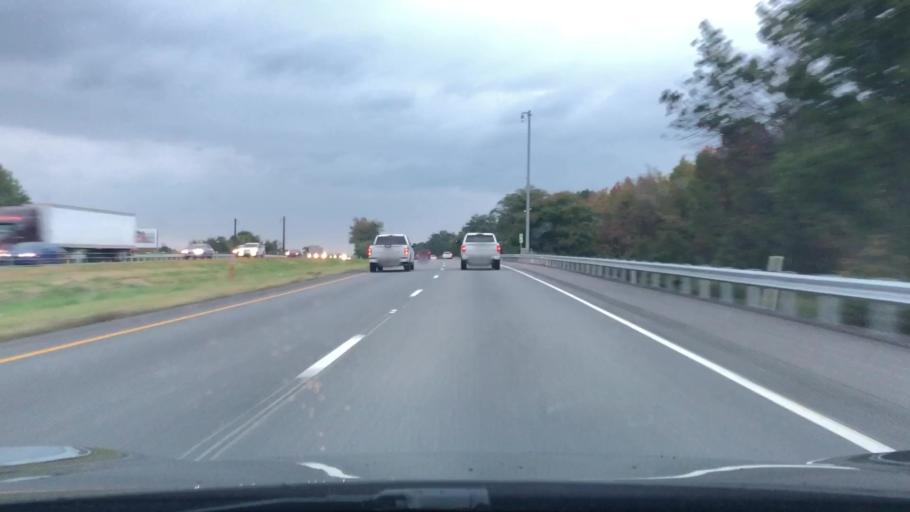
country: US
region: Pennsylvania
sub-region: Bucks County
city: Woodbourne
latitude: 40.2016
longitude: -74.8750
